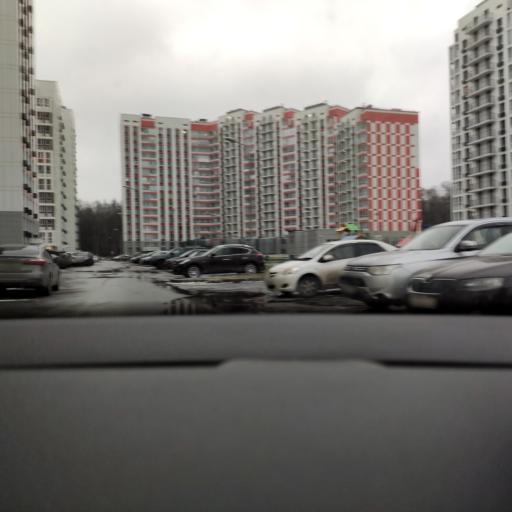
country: RU
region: Moscow
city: Severnyy
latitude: 55.9244
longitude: 37.5488
